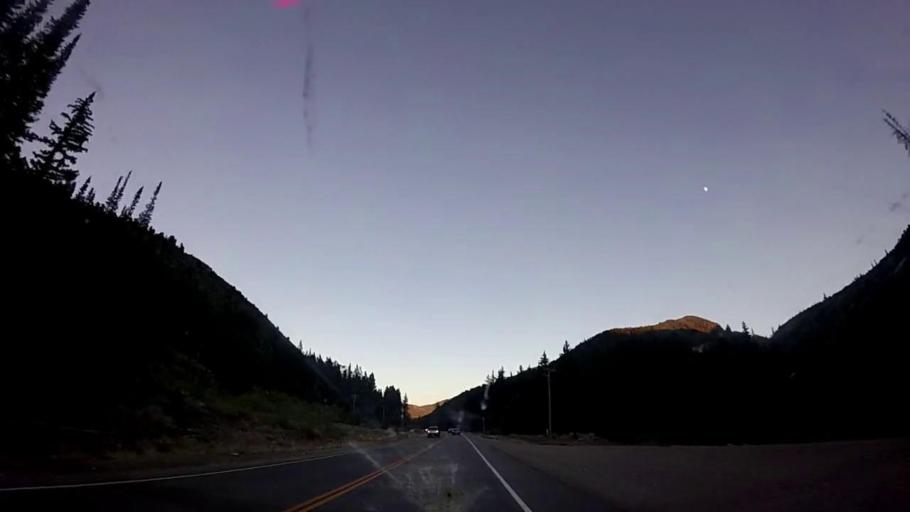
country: US
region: Utah
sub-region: Summit County
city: Summit Park
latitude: 40.6447
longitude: -111.6409
